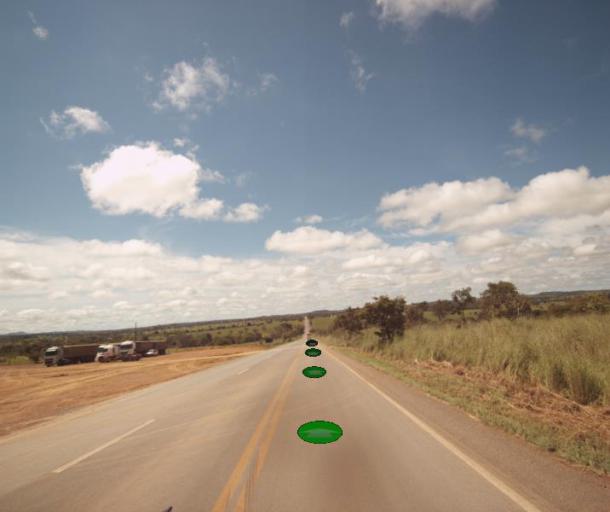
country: BR
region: Goias
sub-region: Padre Bernardo
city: Padre Bernardo
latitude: -15.1551
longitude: -48.3259
